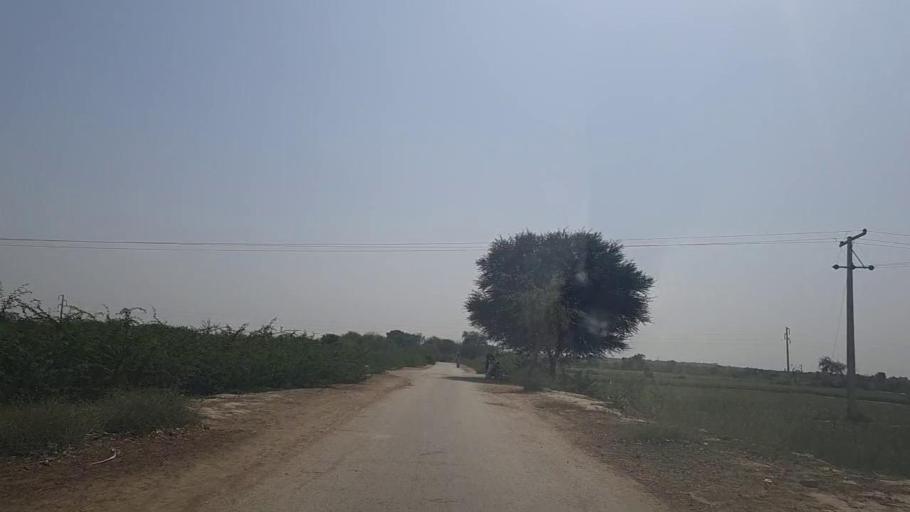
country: PK
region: Sindh
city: Naukot
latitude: 24.8425
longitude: 69.4395
